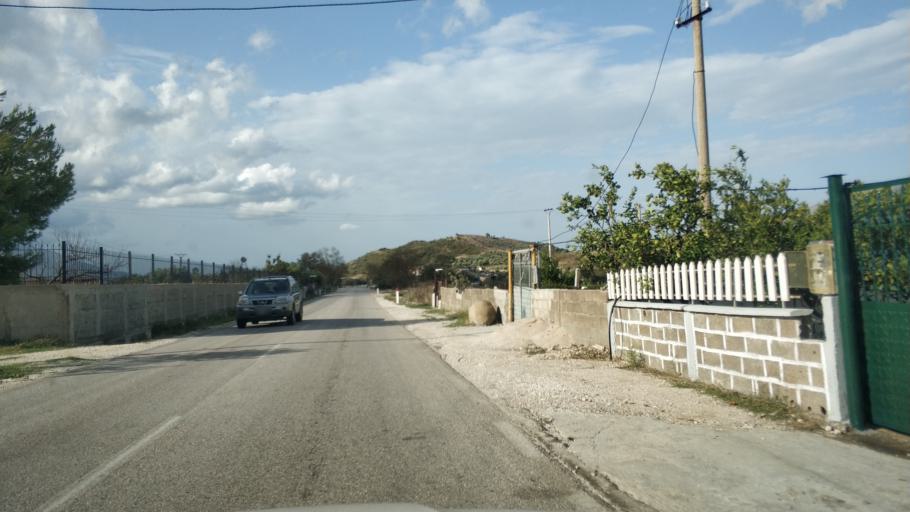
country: AL
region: Vlore
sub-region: Rrethi i Vlores
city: Orikum
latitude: 40.2913
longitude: 19.4920
